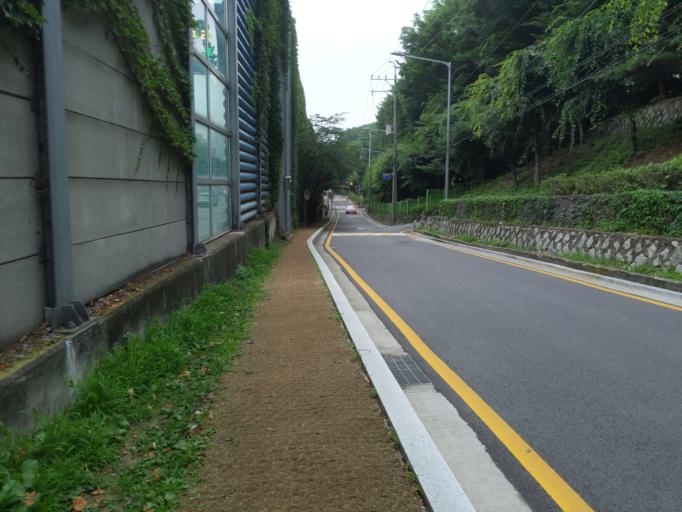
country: KR
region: Seoul
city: Seoul
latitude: 37.5063
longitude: 127.0175
